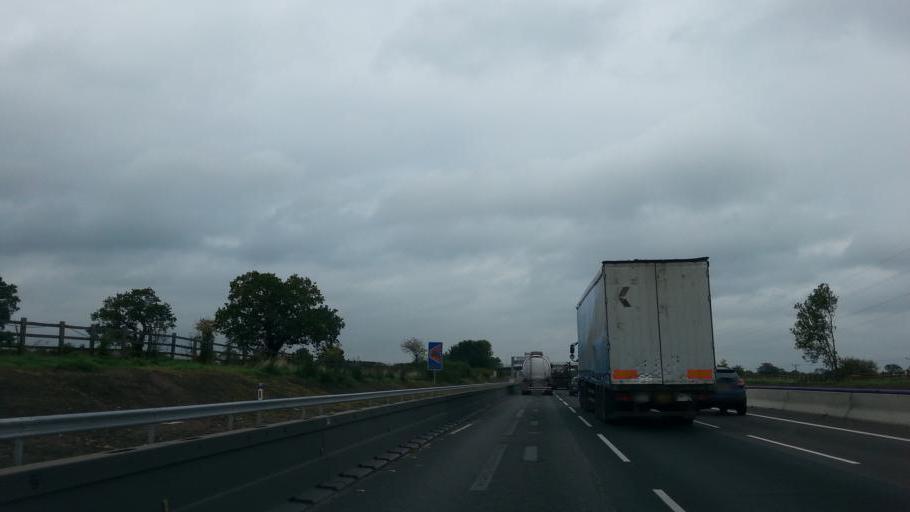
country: GB
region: England
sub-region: Cheshire East
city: Knutsford
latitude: 53.2727
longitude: -2.3991
